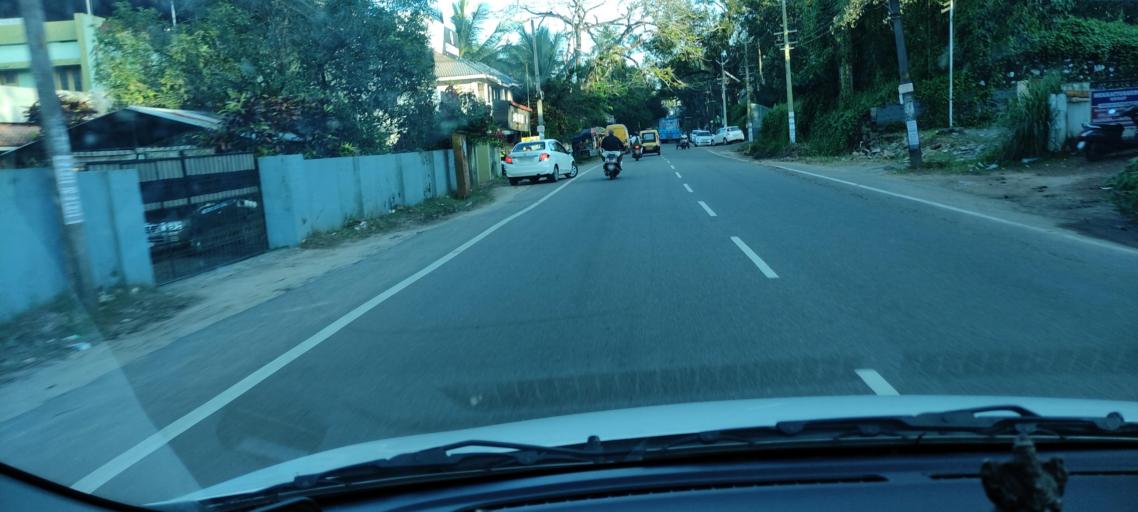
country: IN
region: Kerala
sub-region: Pattanamtitta
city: Adur
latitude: 9.1521
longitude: 76.7442
